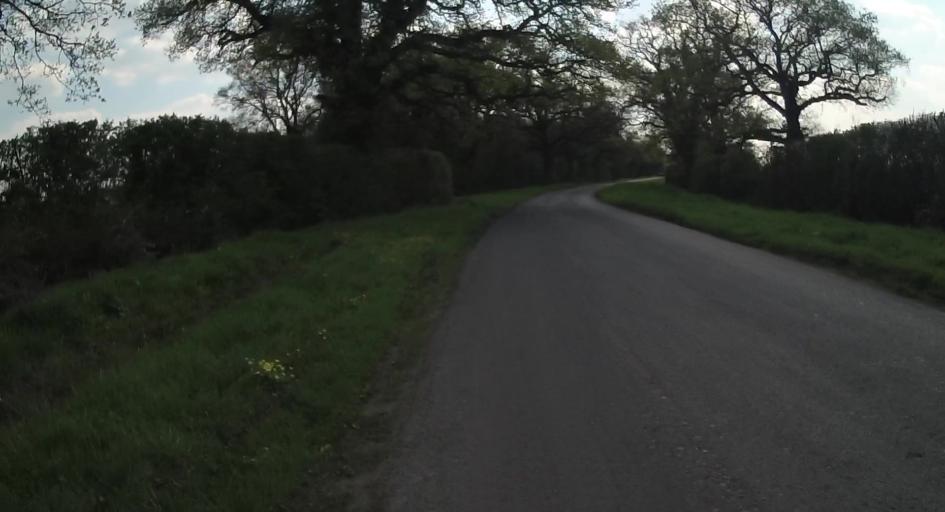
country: GB
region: England
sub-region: West Berkshire
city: Stratfield Mortimer
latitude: 51.3625
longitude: -1.0053
